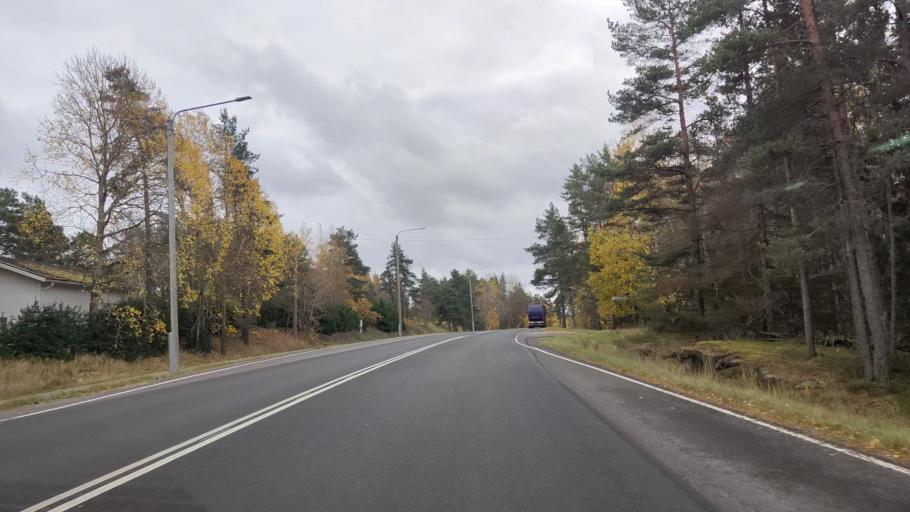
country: FI
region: Varsinais-Suomi
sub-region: Turku
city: Kaarina
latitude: 60.4515
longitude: 22.3720
